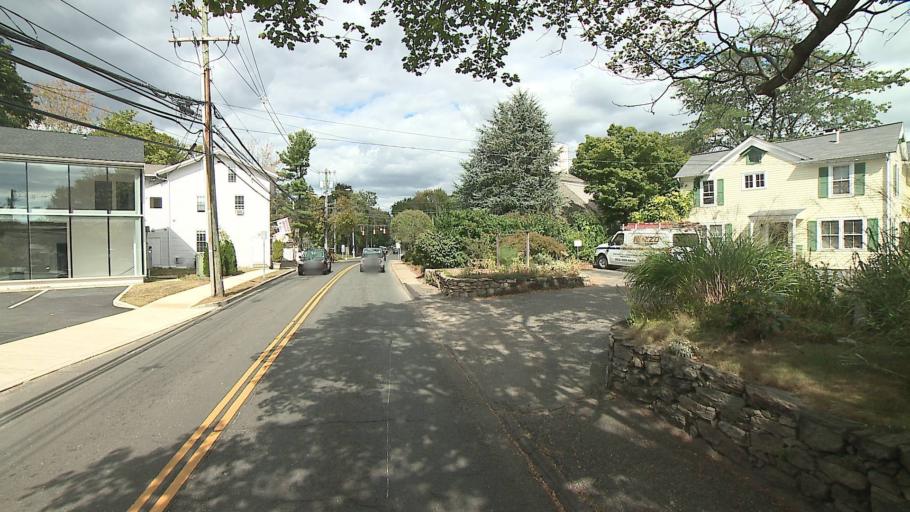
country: US
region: Connecticut
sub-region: Fairfield County
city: Westport
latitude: 41.1240
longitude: -73.3724
